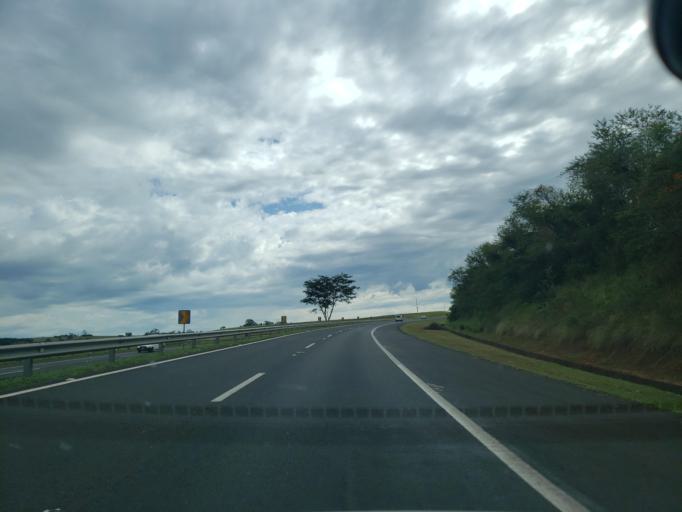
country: BR
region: Sao Paulo
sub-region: Bauru
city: Bauru
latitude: -22.1958
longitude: -49.1986
